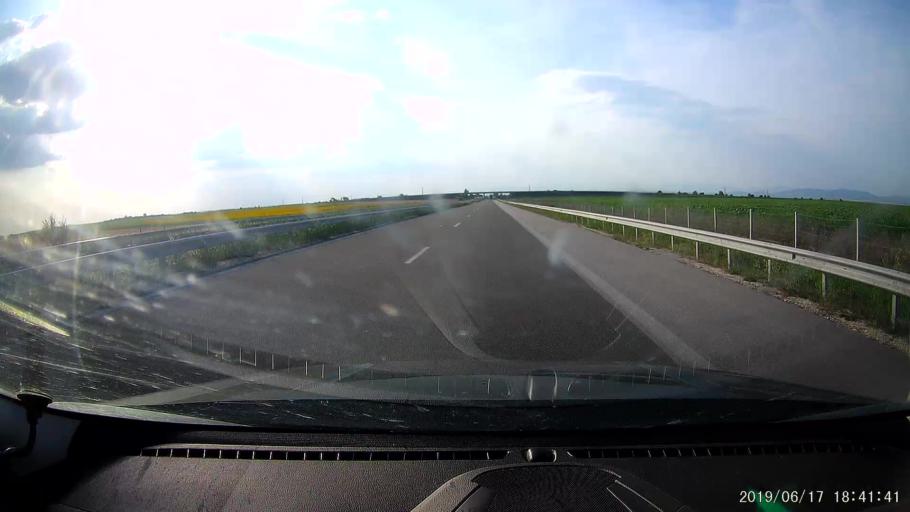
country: BG
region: Stara Zagora
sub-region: Obshtina Chirpan
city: Chirpan
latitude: 42.1769
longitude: 25.2513
